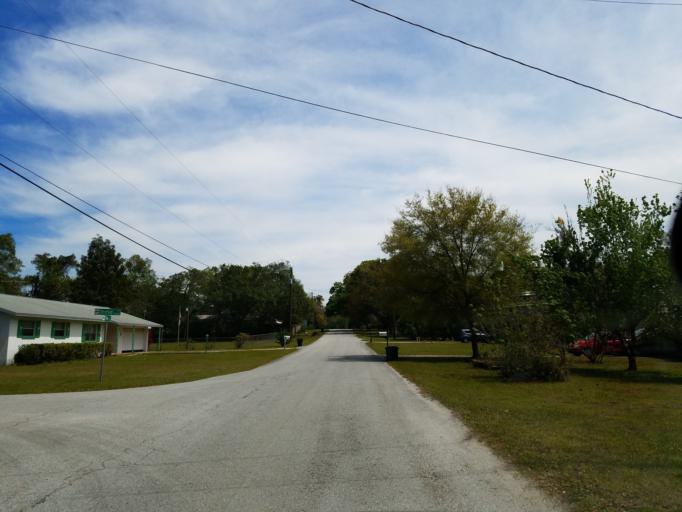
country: US
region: Florida
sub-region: Hillsborough County
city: Thonotosassa
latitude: 28.0696
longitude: -82.3062
